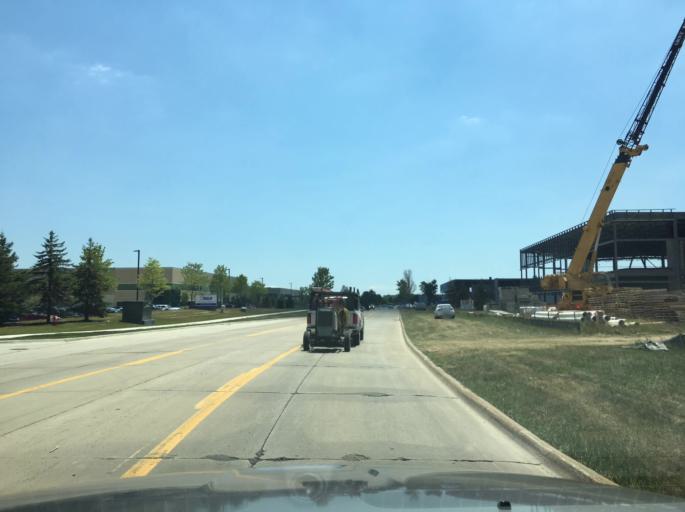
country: US
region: Michigan
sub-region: Macomb County
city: Shelby
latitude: 42.6816
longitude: -83.0127
